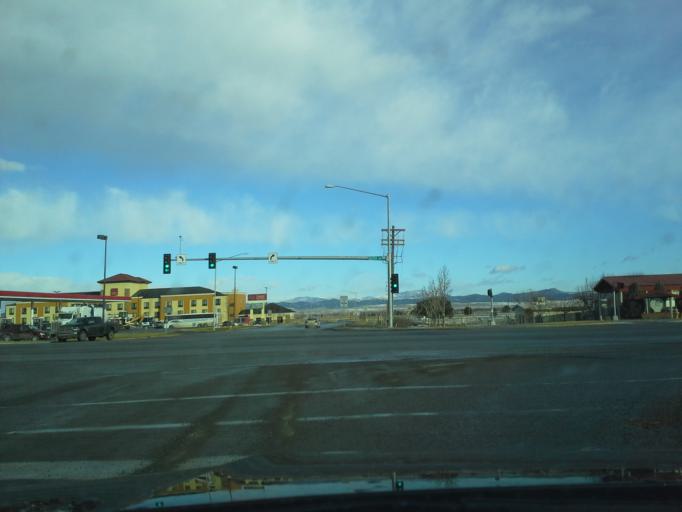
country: US
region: Montana
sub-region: Lewis and Clark County
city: Helena
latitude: 46.6164
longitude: -112.0050
